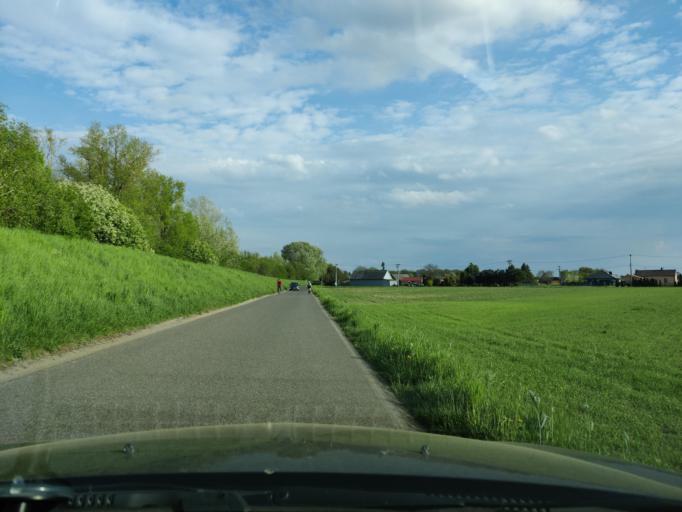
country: PL
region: Masovian Voivodeship
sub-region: Powiat otwocki
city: Jozefow
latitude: 52.1174
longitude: 21.1802
